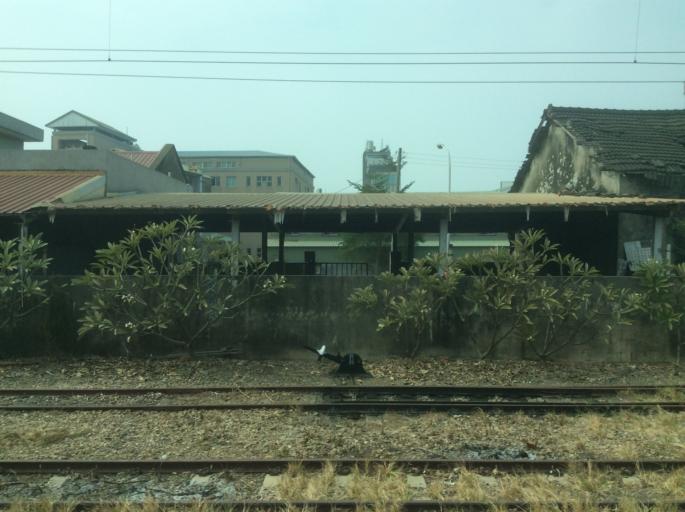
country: TW
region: Taiwan
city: Xinying
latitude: 23.1938
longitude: 120.3193
